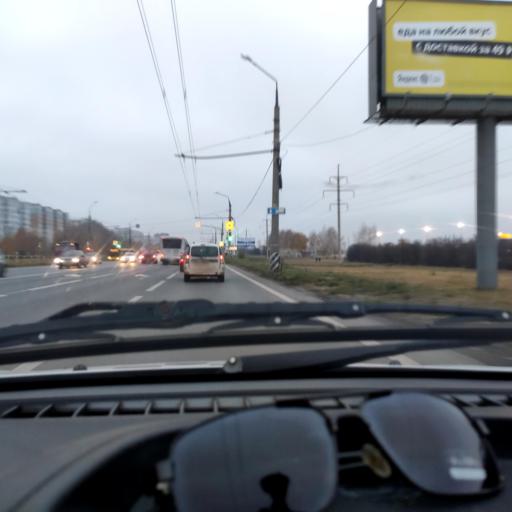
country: RU
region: Samara
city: Tol'yatti
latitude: 53.5489
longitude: 49.3597
